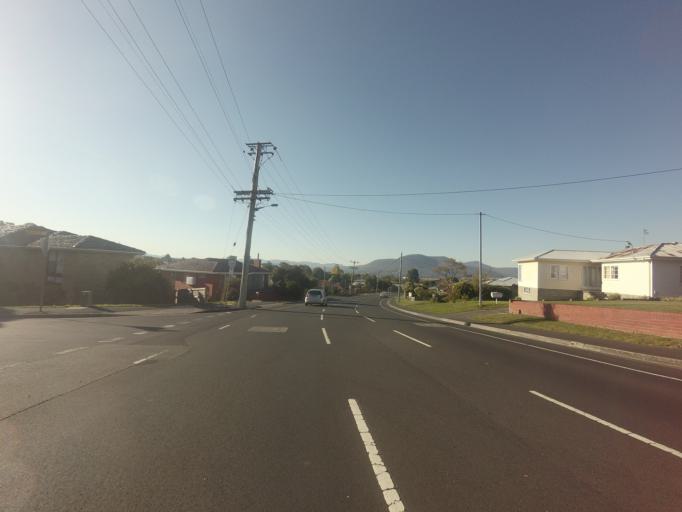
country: AU
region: Tasmania
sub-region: Glenorchy
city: Glenorchy
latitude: -42.8451
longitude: 147.2655
